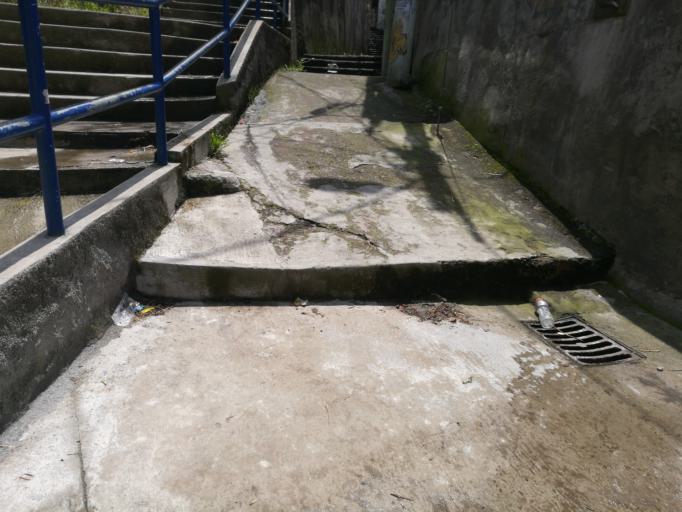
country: EC
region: Pichincha
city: Quito
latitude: -0.2016
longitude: -78.4786
